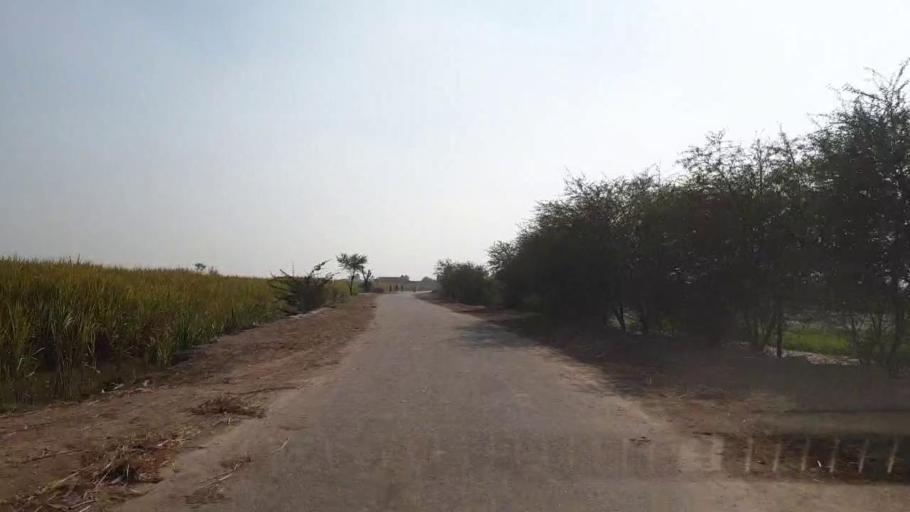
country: PK
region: Sindh
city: Tando Adam
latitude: 25.6633
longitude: 68.5766
